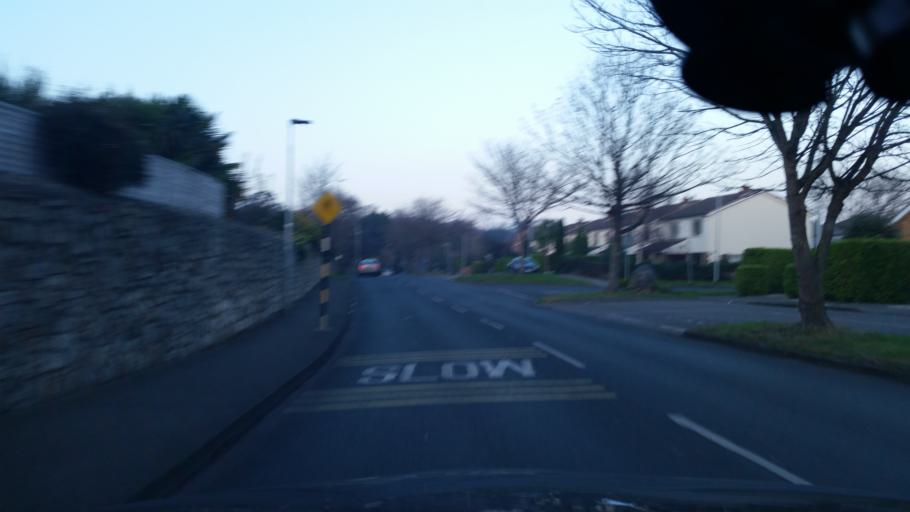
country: IE
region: Leinster
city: Loughlinstown
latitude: 53.2455
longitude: -6.1204
